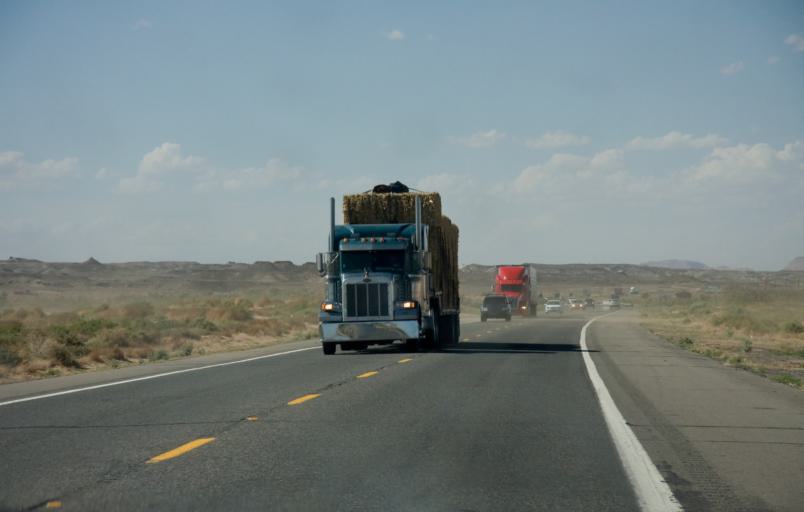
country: US
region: Arizona
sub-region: Coconino County
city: Tuba City
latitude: 36.0142
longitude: -111.3956
